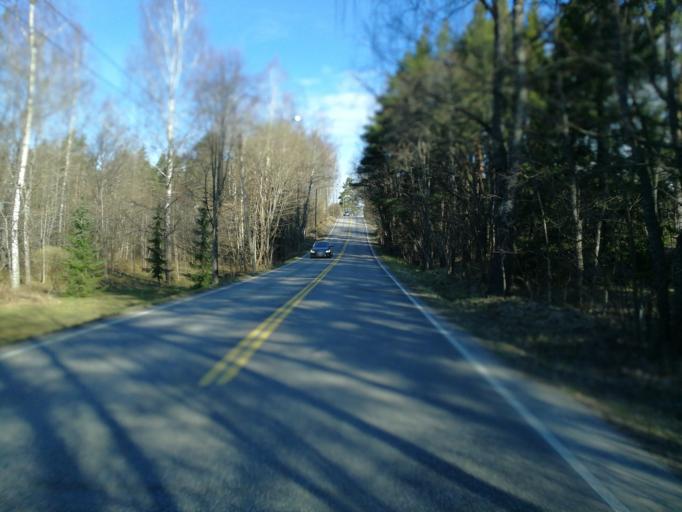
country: FI
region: Uusimaa
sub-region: Helsinki
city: Kirkkonummi
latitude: 60.2166
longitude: 24.4776
